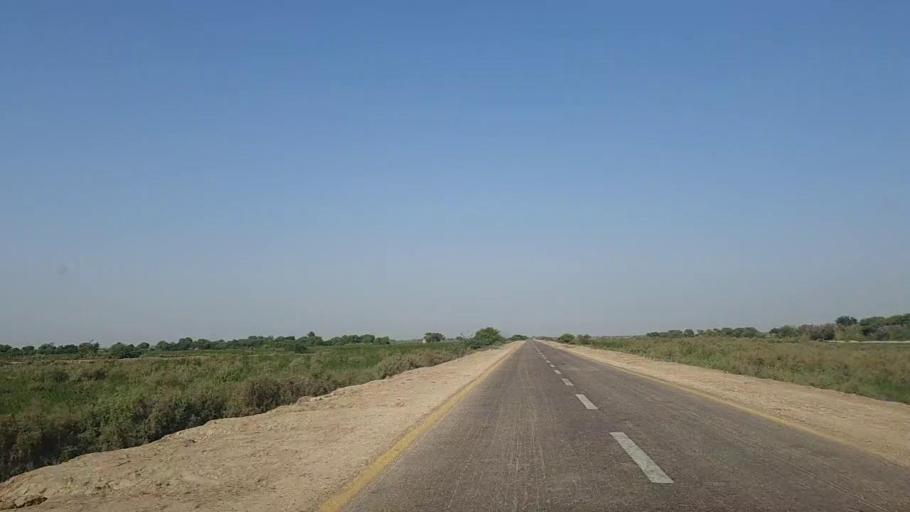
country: PK
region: Sindh
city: Jati
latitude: 24.3914
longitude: 68.2878
